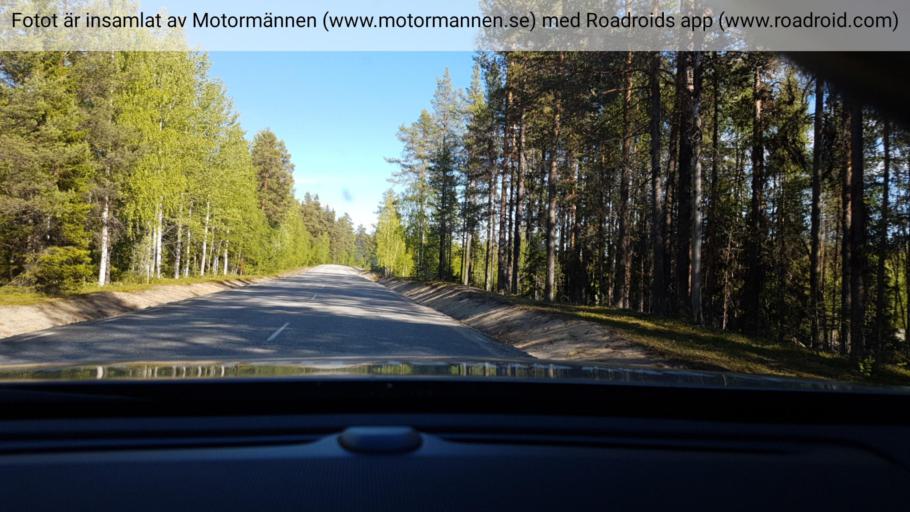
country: SE
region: Vaesterbotten
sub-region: Norsjo Kommun
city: Norsjoe
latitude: 64.6963
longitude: 19.1809
